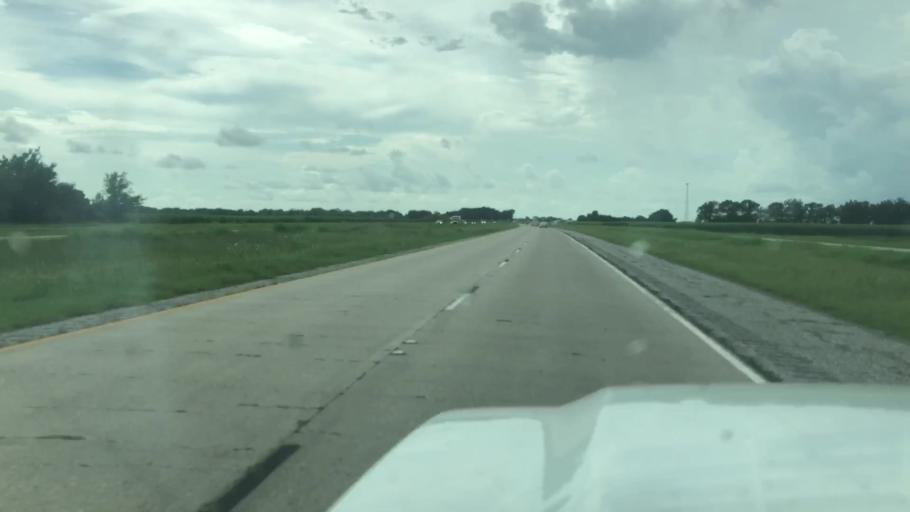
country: US
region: Louisiana
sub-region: Saint Mary Parish
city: Baldwin
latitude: 29.8578
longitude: -91.6131
